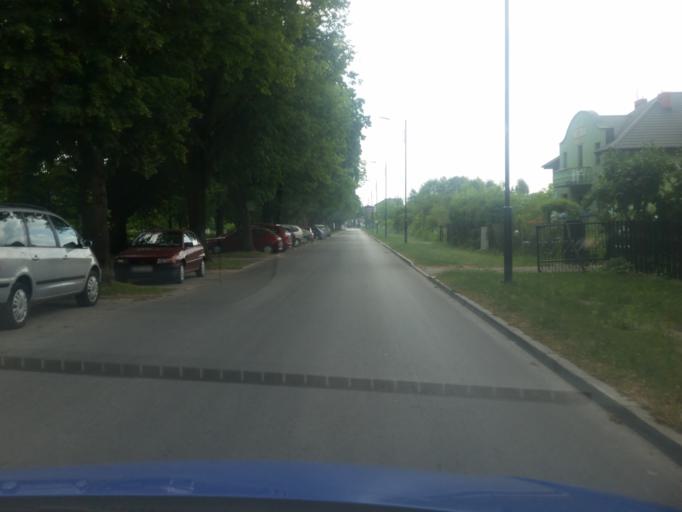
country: PL
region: Swietokrzyskie
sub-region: Powiat buski
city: Busko-Zdroj
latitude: 50.4602
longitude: 20.7131
